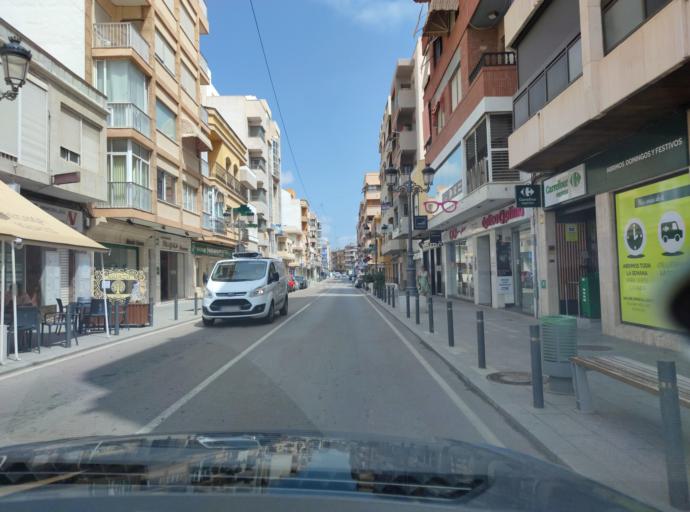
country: ES
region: Valencia
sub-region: Provincia de Alicante
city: Guardamar del Segura
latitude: 38.0905
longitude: -0.6547
